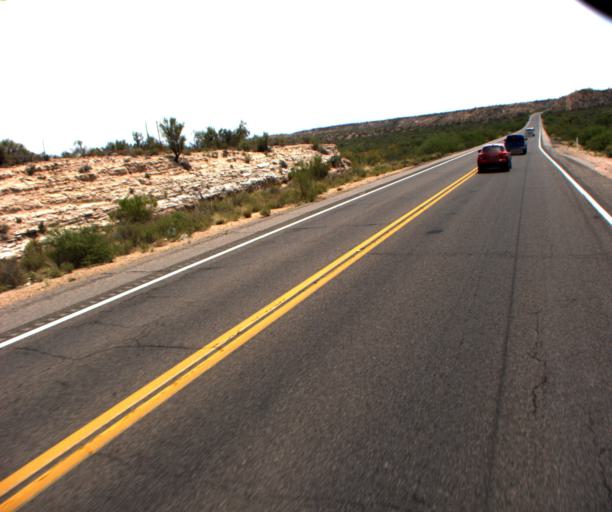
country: US
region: Arizona
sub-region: Gila County
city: San Carlos
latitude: 33.3452
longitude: -110.6178
